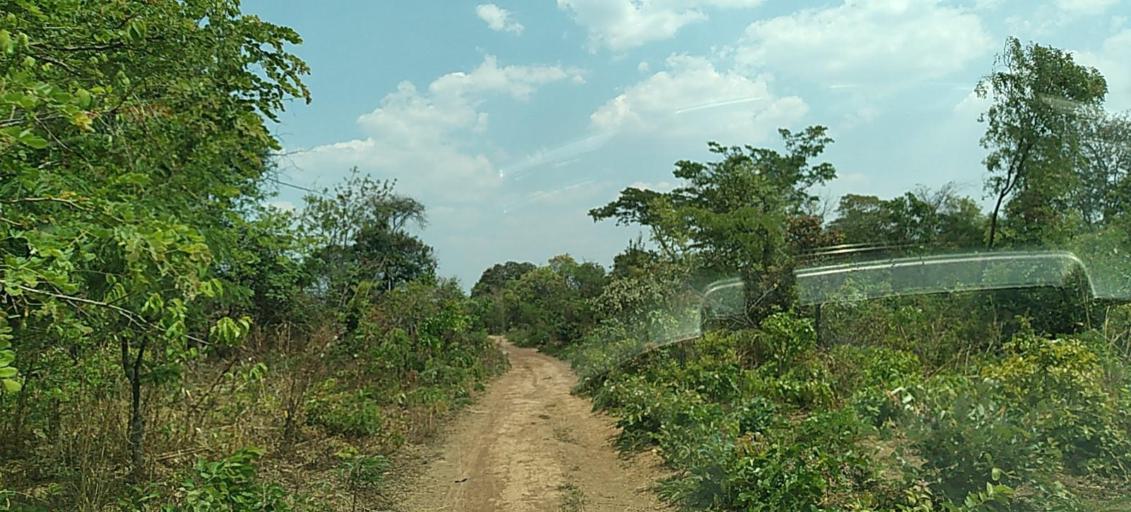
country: CD
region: Katanga
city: Kipushi
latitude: -11.9849
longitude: 27.4159
